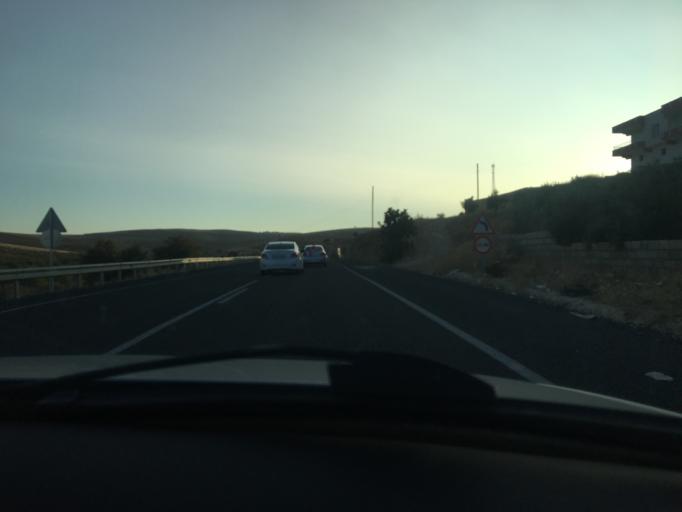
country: TR
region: Sanliurfa
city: Halfeti
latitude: 37.2029
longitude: 37.9698
